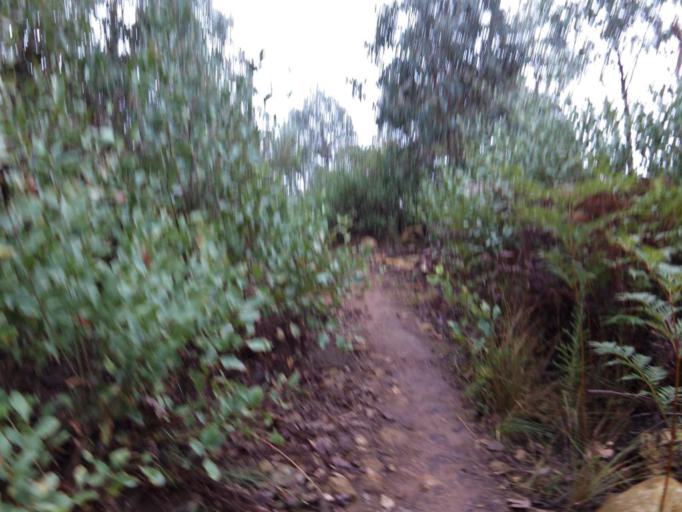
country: AU
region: Victoria
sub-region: Yarra Ranges
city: Millgrove
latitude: -37.5292
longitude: 145.7622
